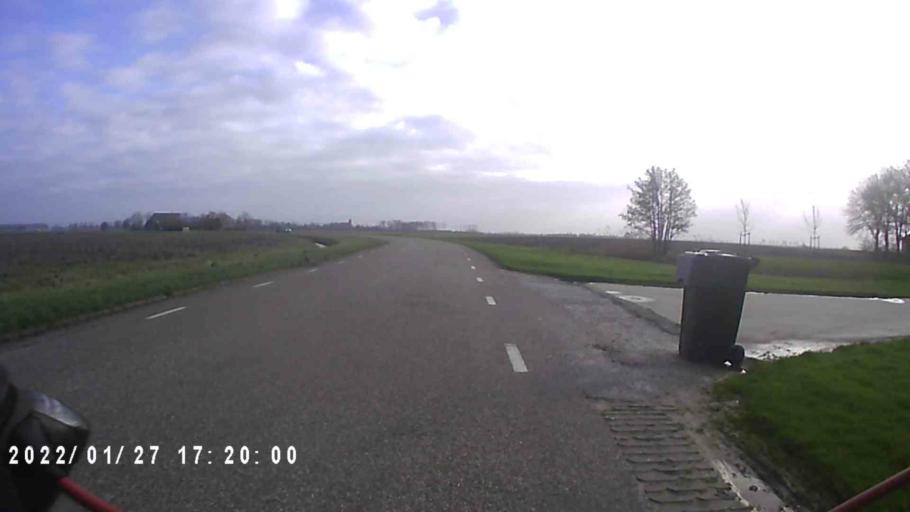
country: NL
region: Friesland
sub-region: Gemeente Dongeradeel
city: Anjum
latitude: 53.3851
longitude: 6.1120
